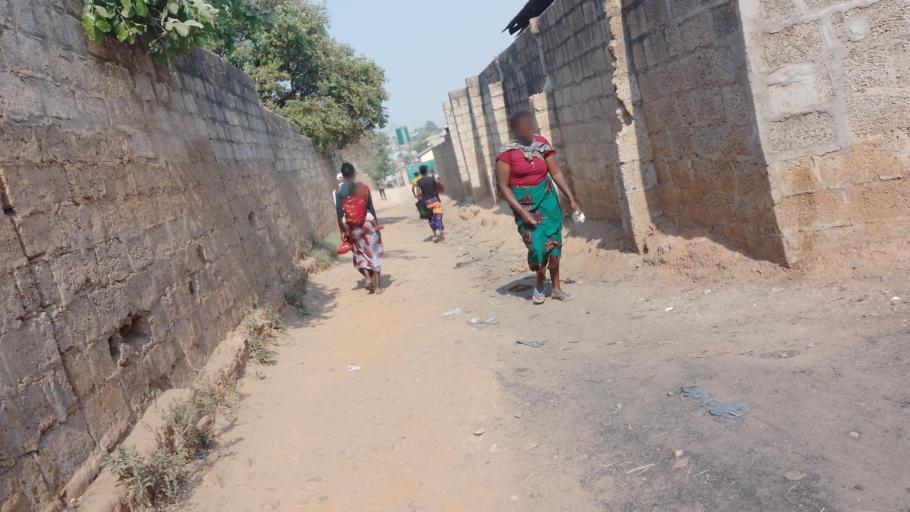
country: ZM
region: Lusaka
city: Lusaka
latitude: -15.4022
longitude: 28.3675
